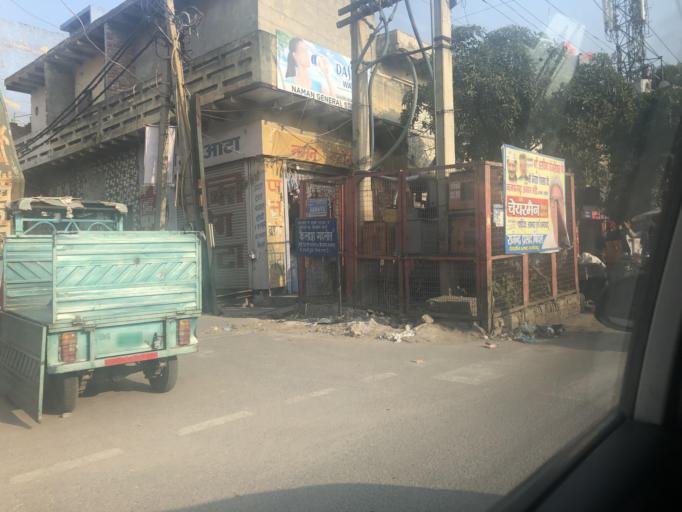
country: IN
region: Haryana
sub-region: Jhajjar
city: Bahadurgarh
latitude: 28.6185
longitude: 76.9749
